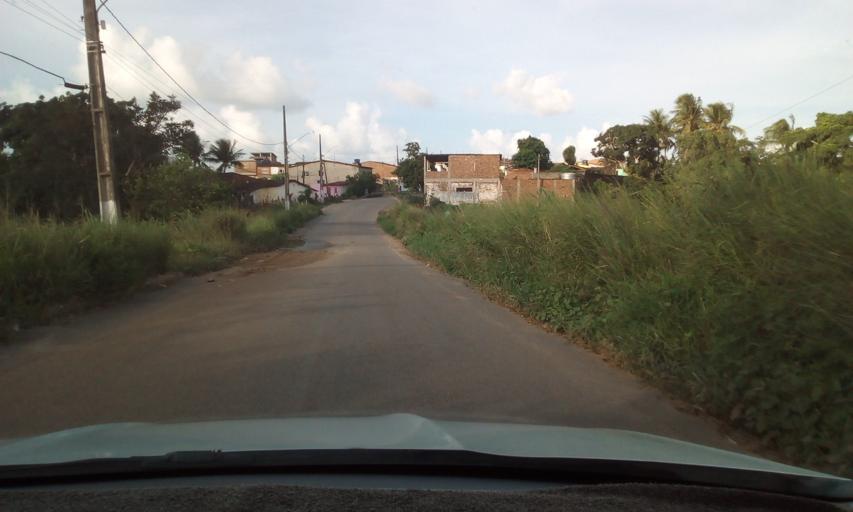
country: BR
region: Pernambuco
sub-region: Gloria Do Goita
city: Gloria do Goita
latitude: -7.9961
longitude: -35.2140
